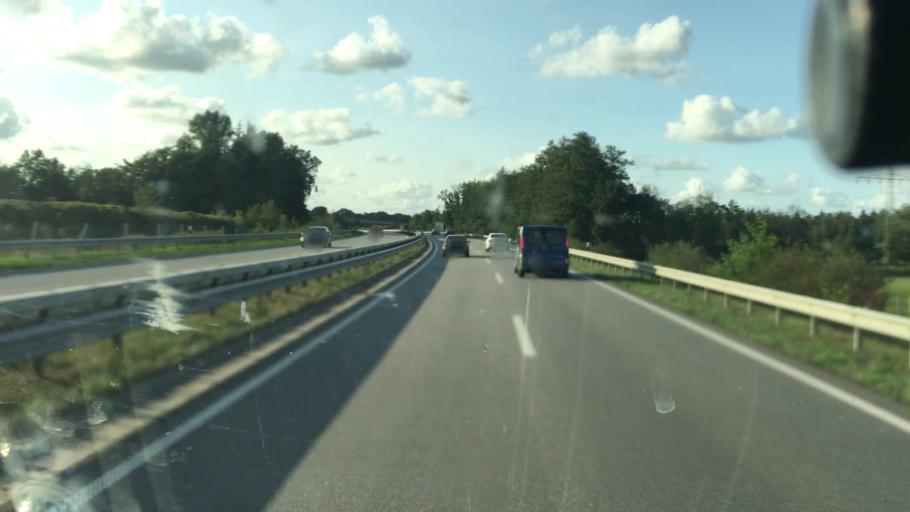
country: DE
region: Lower Saxony
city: Schortens
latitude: 53.5395
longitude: 7.9755
